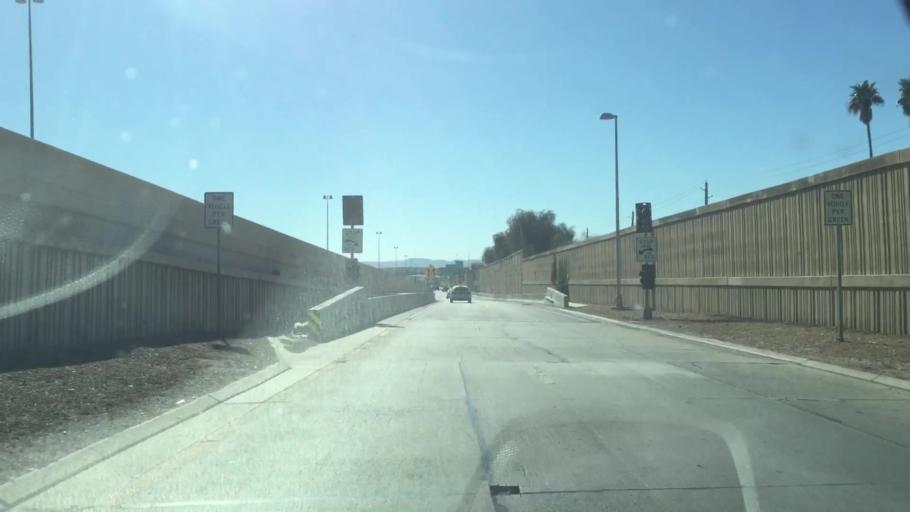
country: US
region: Arizona
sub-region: Maricopa County
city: Phoenix
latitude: 33.4764
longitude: -112.0388
